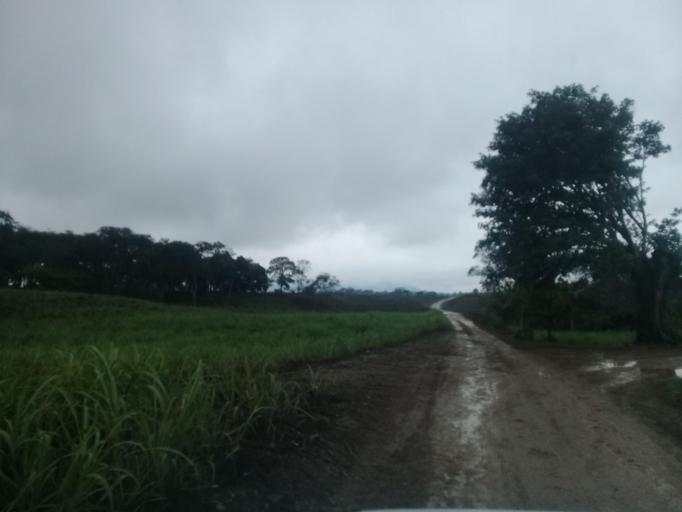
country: MX
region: Veracruz
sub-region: Amatlan de los Reyes
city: Centro de Readaptacion Social
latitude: 18.8198
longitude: -96.9416
